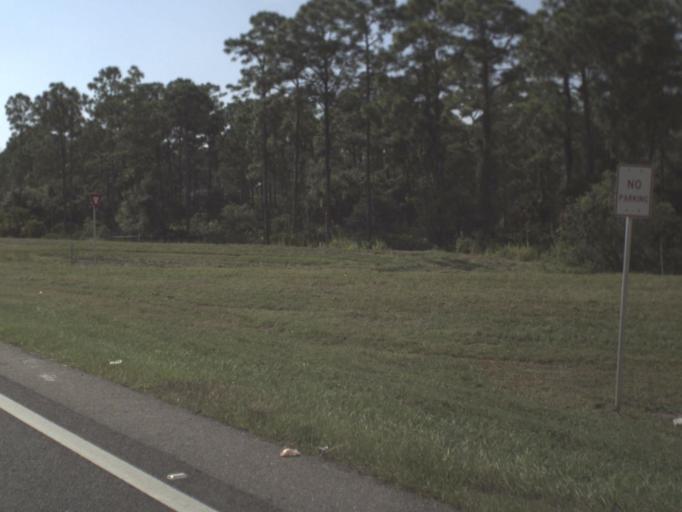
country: US
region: Florida
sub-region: Sarasota County
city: Plantation
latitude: 27.1110
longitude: -82.3489
